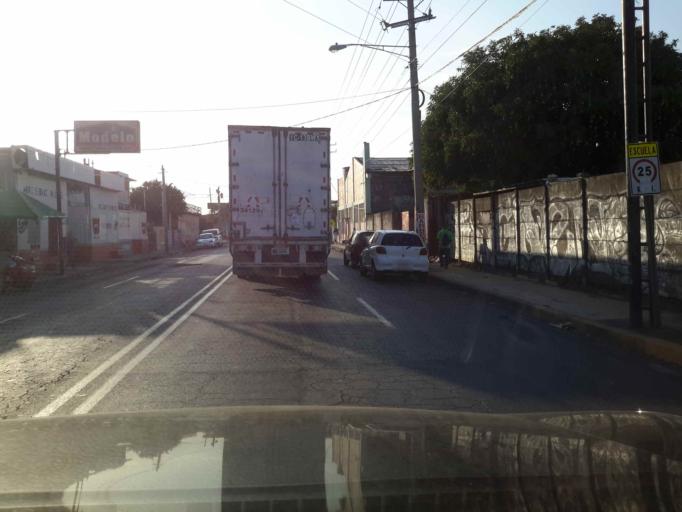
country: NI
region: Managua
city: Managua
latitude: 12.1576
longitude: -86.2886
